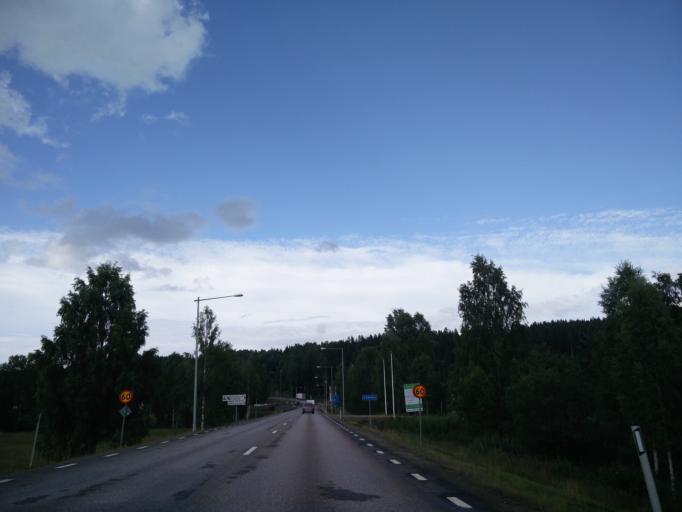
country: SE
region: Vaermland
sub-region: Hagfors Kommun
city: Ekshaerad
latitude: 60.4207
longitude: 13.2546
